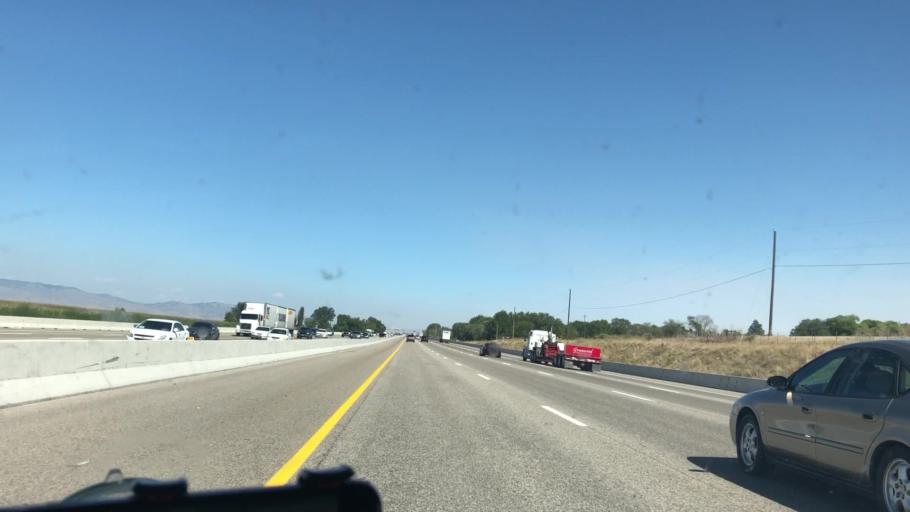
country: US
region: Idaho
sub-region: Ada County
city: Meridian
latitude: 43.5981
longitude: -116.4832
